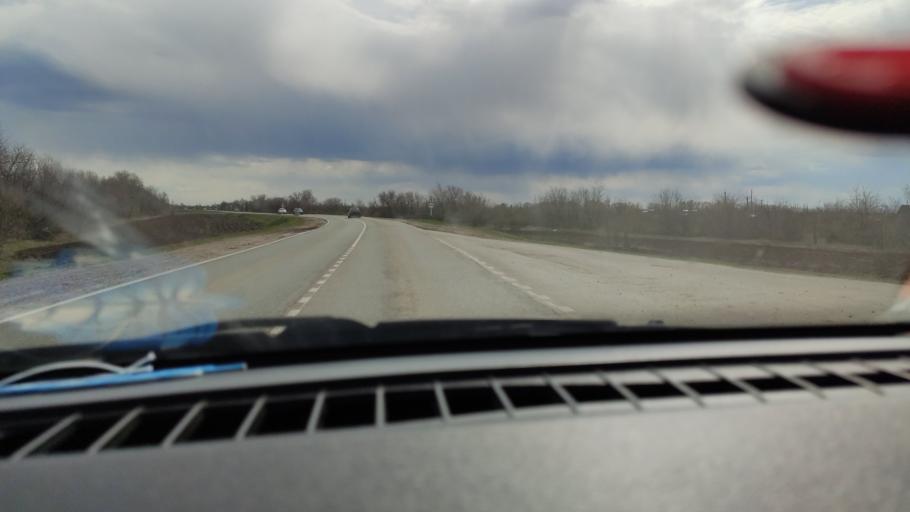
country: RU
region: Saratov
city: Privolzhskiy
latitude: 51.3392
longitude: 46.0407
